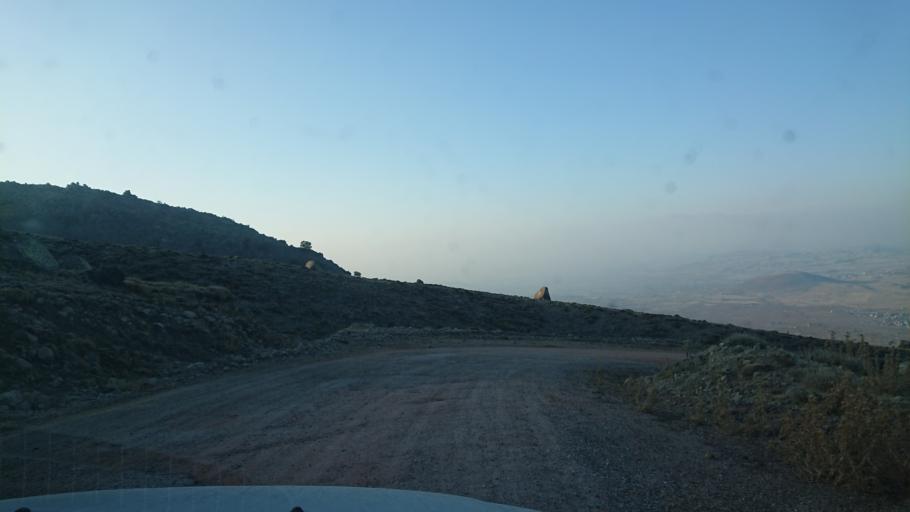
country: TR
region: Aksaray
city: Taspinar
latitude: 38.1629
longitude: 34.1765
